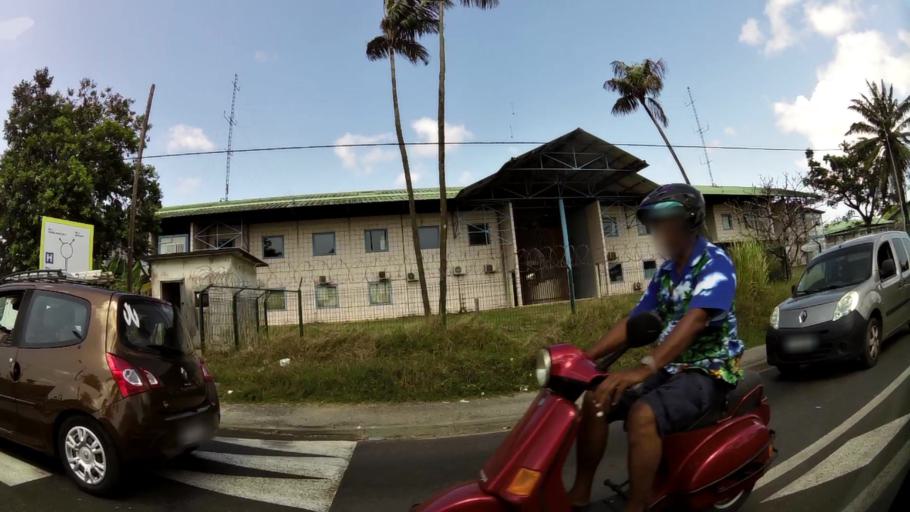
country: GF
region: Guyane
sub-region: Guyane
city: Cayenne
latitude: 4.9220
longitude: -52.3227
